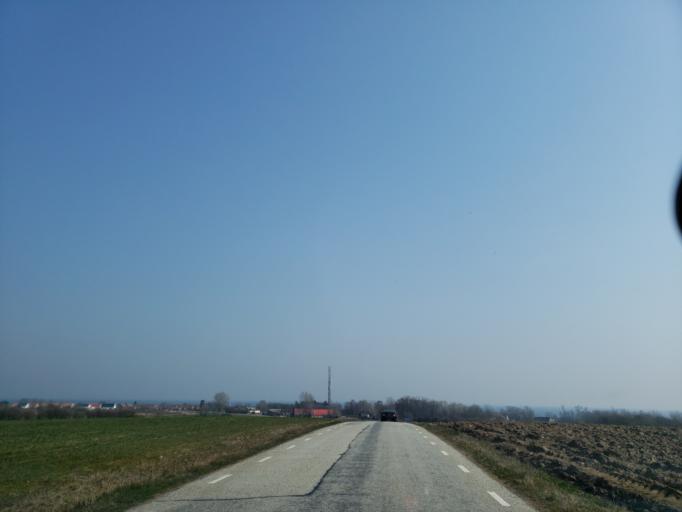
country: SE
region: Skane
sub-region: Simrishamns Kommun
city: Simrishamn
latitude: 55.5110
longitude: 14.3315
